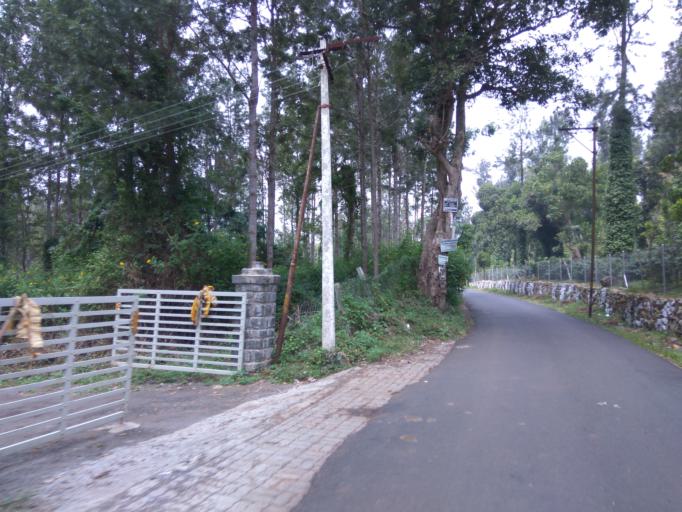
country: IN
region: Tamil Nadu
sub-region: Salem
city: Salem
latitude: 11.7756
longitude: 78.2249
